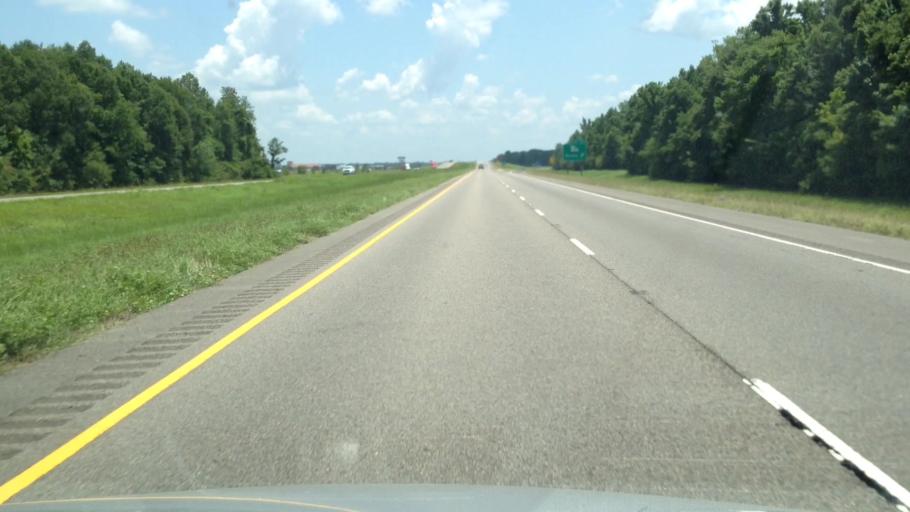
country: US
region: Louisiana
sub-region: Avoyelles Parish
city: Bunkie
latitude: 30.9582
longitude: -92.2814
